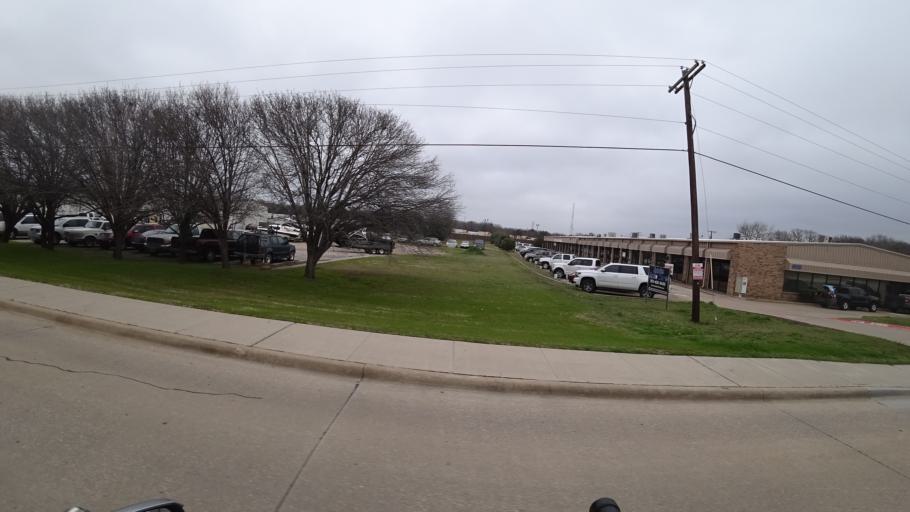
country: US
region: Texas
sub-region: Denton County
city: Lewisville
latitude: 33.0542
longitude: -96.9982
